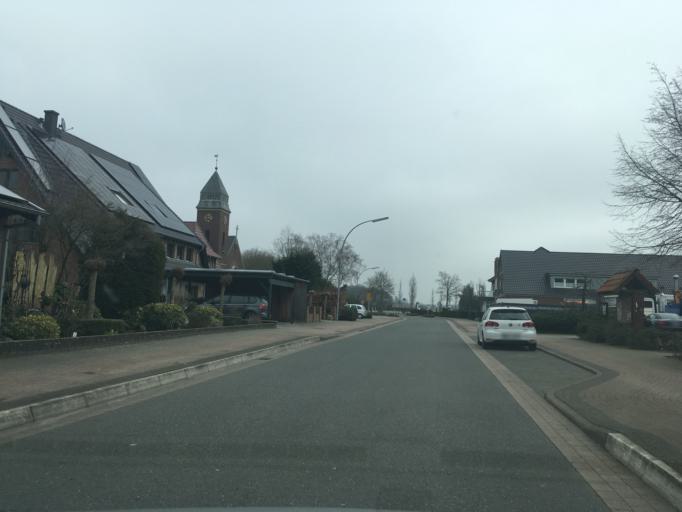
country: DE
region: North Rhine-Westphalia
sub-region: Regierungsbezirk Munster
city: Rhede
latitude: 51.8650
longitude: 6.7354
